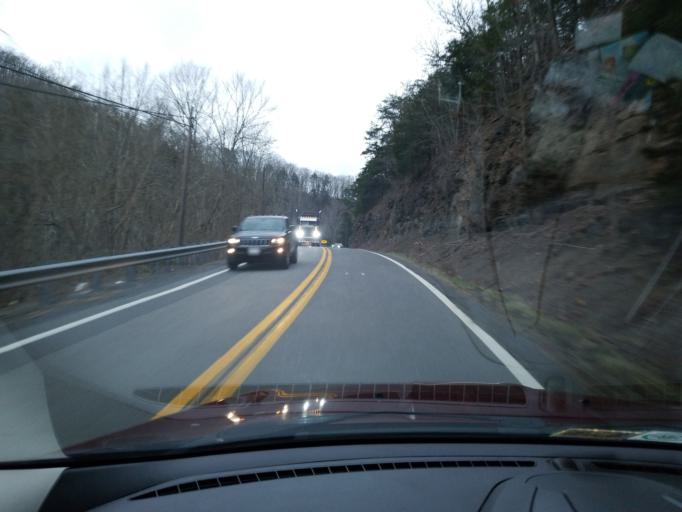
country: US
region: West Virginia
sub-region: Monroe County
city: Union
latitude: 37.5257
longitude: -80.6115
